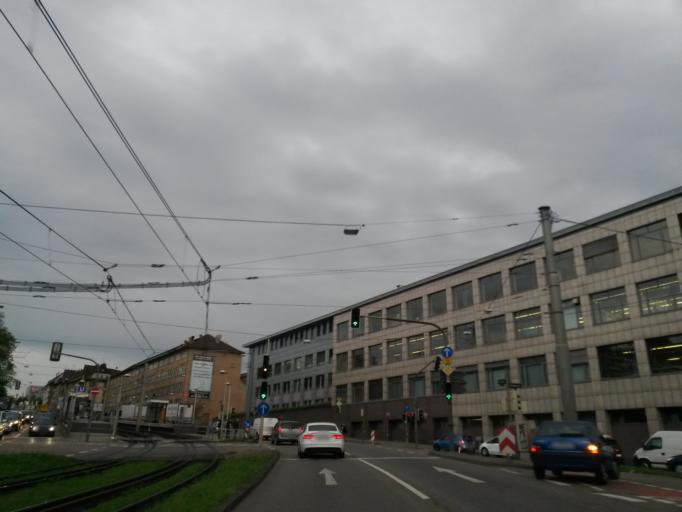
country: DE
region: Baden-Wuerttemberg
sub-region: Regierungsbezirk Stuttgart
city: Stuttgart-Ost
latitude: 48.8081
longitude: 9.2055
